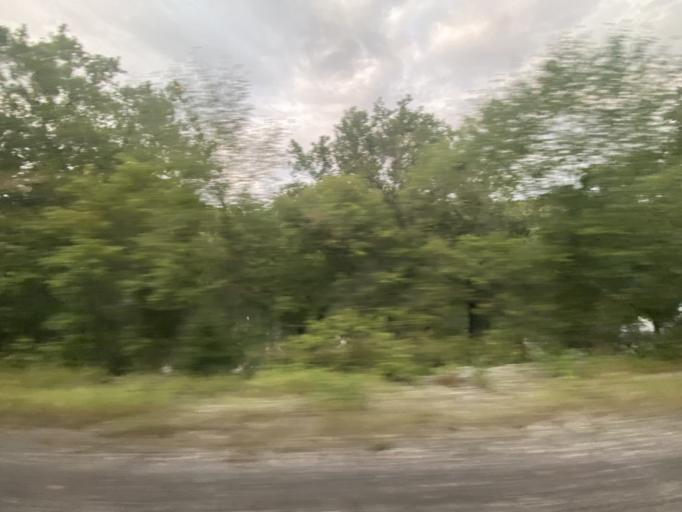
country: US
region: West Virginia
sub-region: Mineral County
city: Fort Ashby
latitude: 39.5291
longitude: -78.5896
